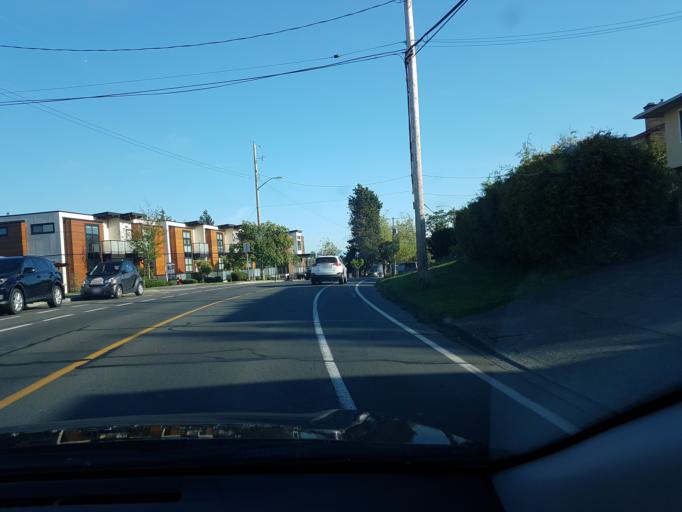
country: CA
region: British Columbia
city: Oak Bay
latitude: 48.4736
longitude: -123.3345
